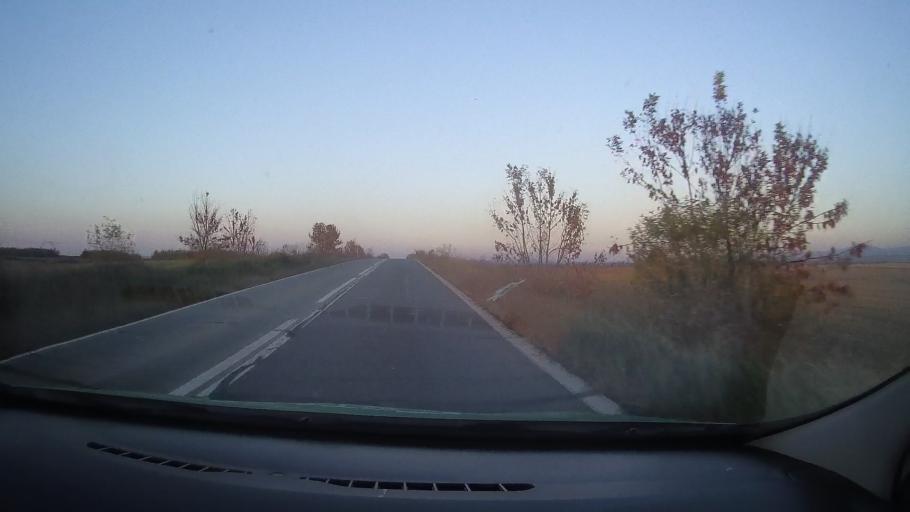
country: RO
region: Timis
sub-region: Comuna Manastiur
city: Manastiur
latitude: 45.8194
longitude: 22.0804
